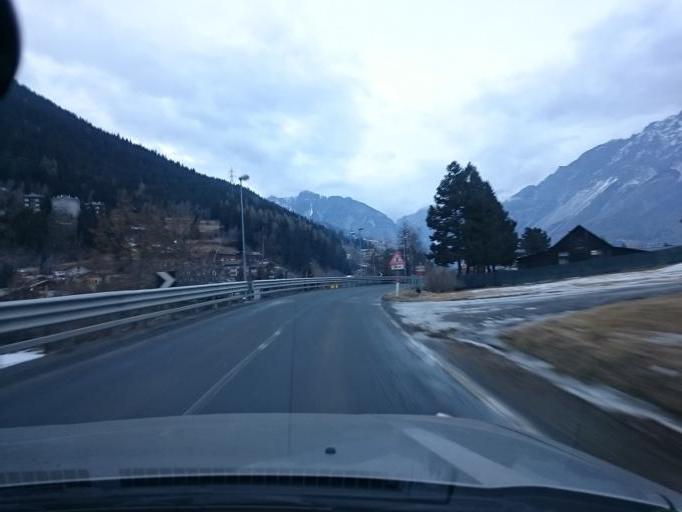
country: IT
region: Lombardy
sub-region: Provincia di Sondrio
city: Cepina
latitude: 46.4385
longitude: 10.3581
